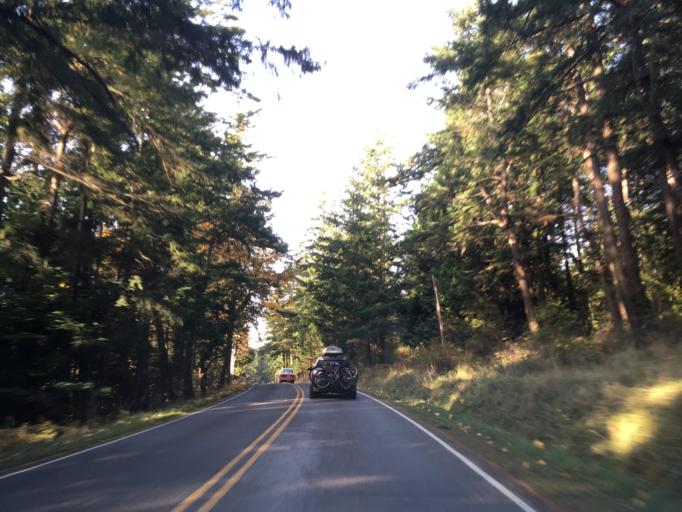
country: US
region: Washington
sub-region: San Juan County
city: Friday Harbor
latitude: 48.6855
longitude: -122.8818
